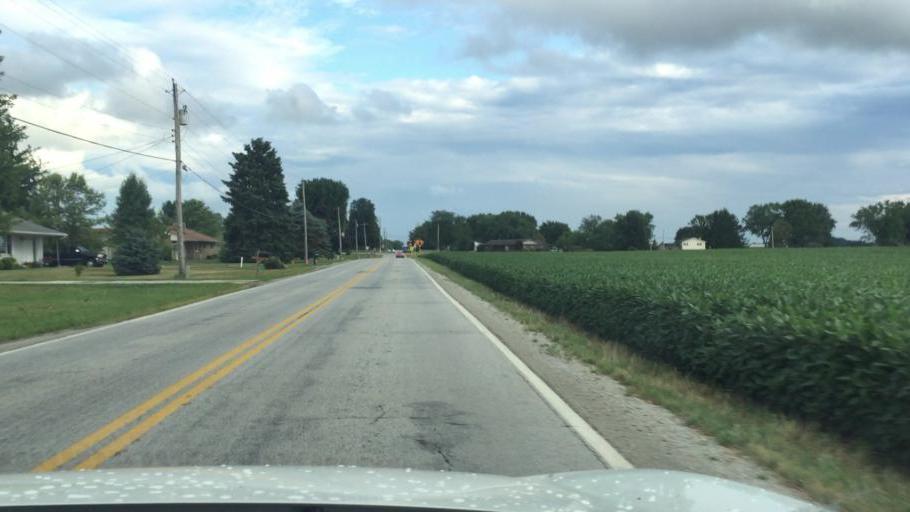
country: US
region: Ohio
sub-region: Clark County
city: Lisbon
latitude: 39.9446
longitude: -83.6819
